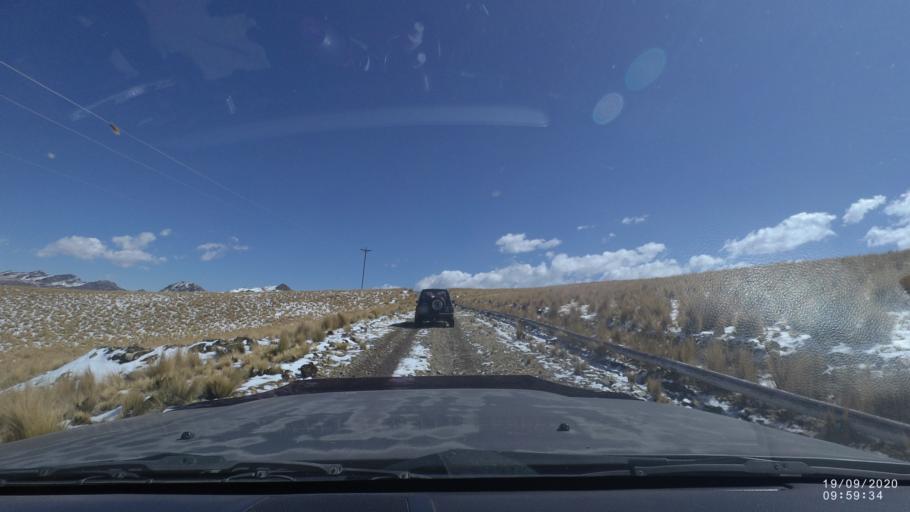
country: BO
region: Cochabamba
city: Cochabamba
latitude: -17.3072
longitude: -66.0883
